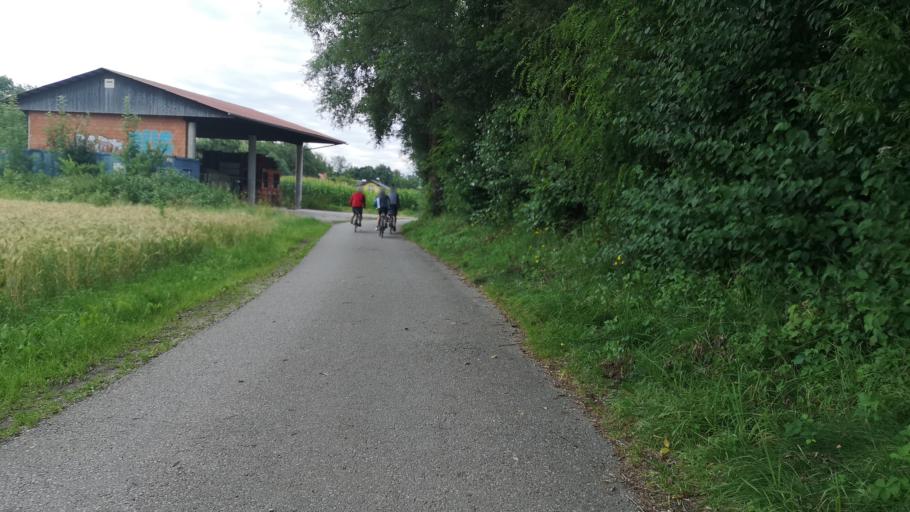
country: AT
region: Styria
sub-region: Politischer Bezirk Graz-Umgebung
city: Gossendorf
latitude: 46.9908
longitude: 15.4645
